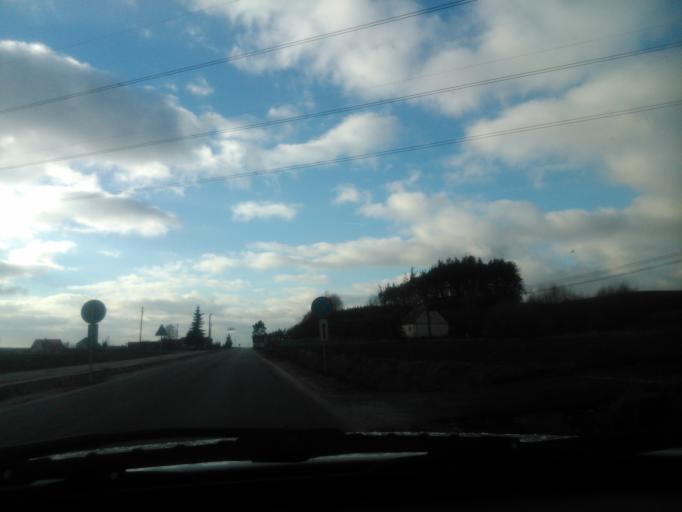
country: PL
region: Kujawsko-Pomorskie
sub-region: Powiat golubsko-dobrzynski
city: Golub-Dobrzyn
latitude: 53.1327
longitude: 19.0930
